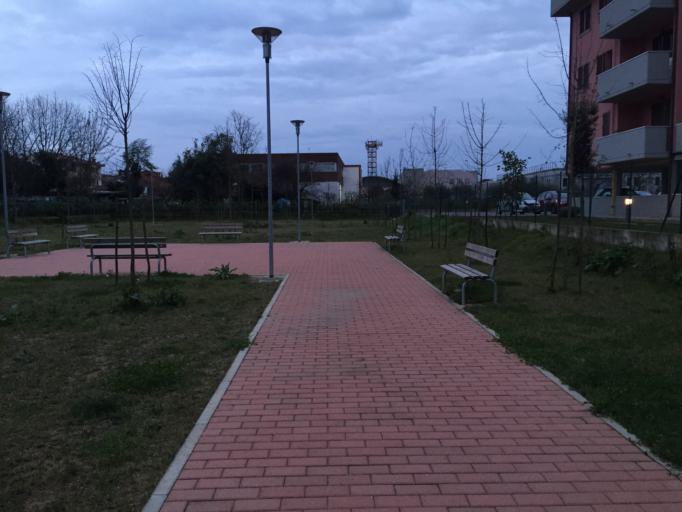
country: IT
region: Tuscany
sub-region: Provincia di Prato
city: Fornacelle
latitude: 43.8858
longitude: 11.0484
